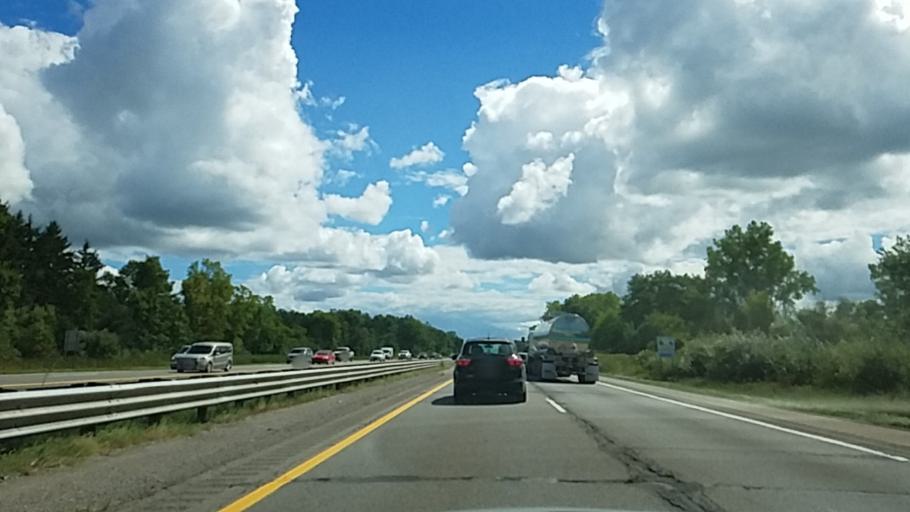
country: US
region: Michigan
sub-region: Livingston County
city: Whitmore Lake
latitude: 42.3628
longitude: -83.7495
